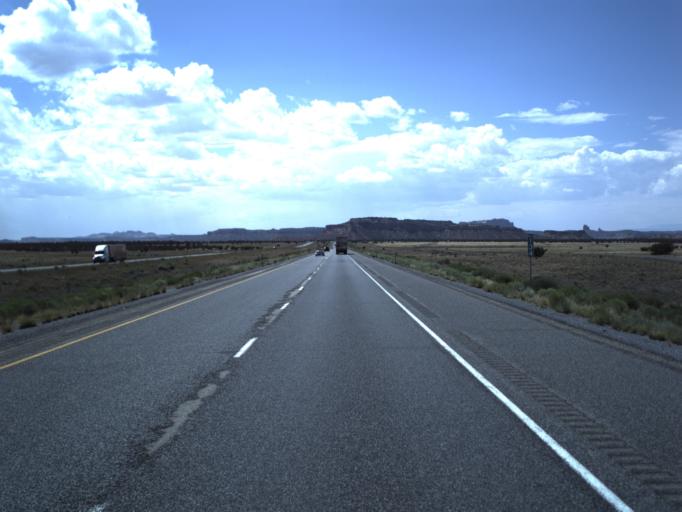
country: US
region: Utah
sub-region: Emery County
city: Castle Dale
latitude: 38.8948
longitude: -110.6168
